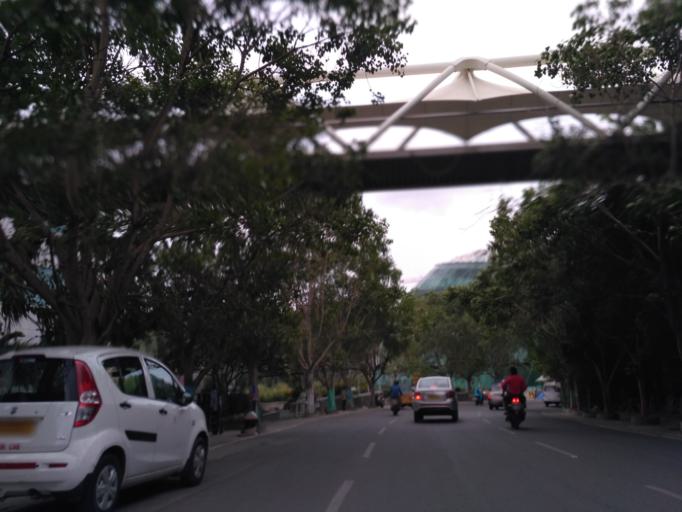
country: IN
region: Telangana
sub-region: Rangareddi
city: Kukatpalli
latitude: 17.4327
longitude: 78.3876
